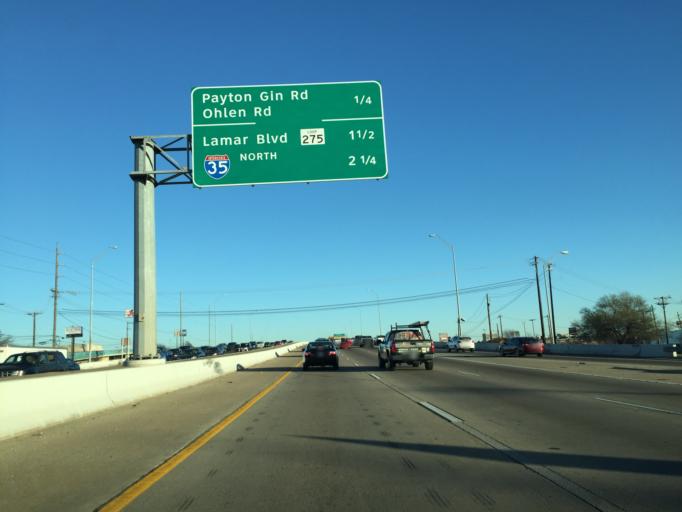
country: US
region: Texas
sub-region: Williamson County
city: Jollyville
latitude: 30.3748
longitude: -97.7298
